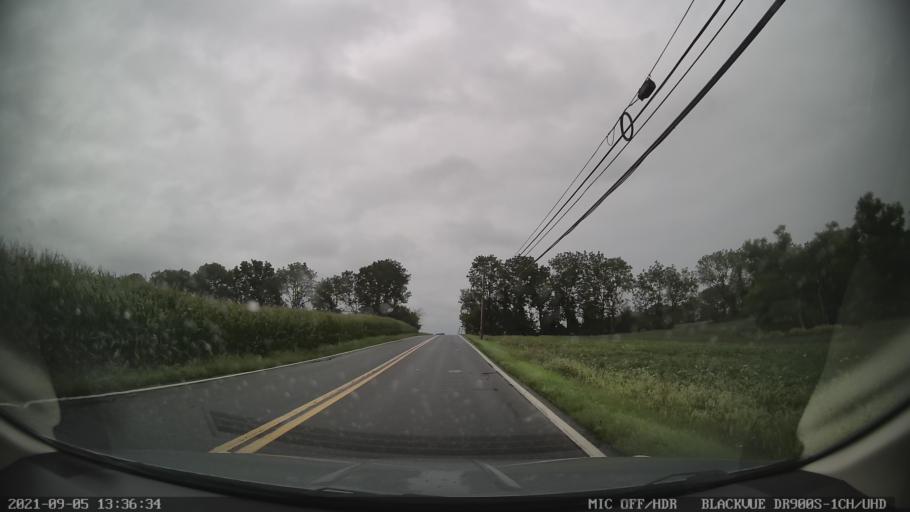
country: US
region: Pennsylvania
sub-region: Lehigh County
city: Breinigsville
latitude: 40.5789
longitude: -75.6538
